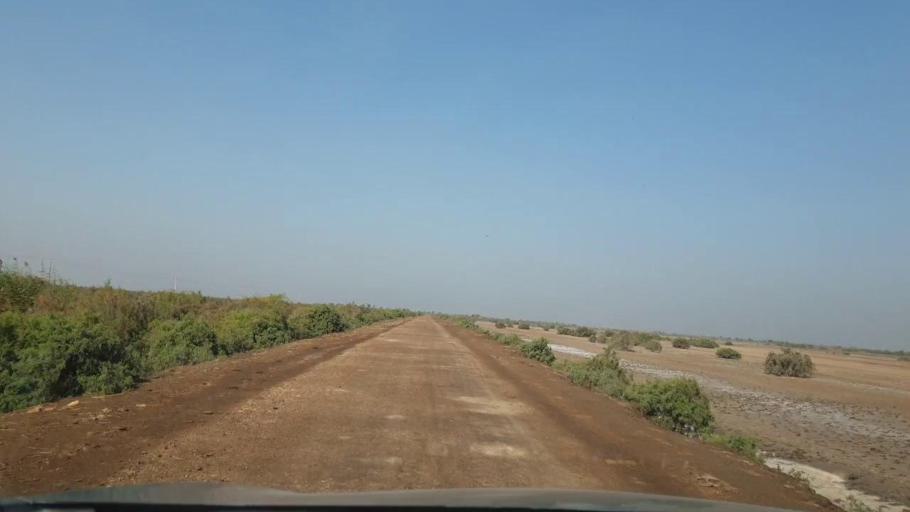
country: PK
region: Sindh
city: Berani
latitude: 25.6958
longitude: 68.8743
